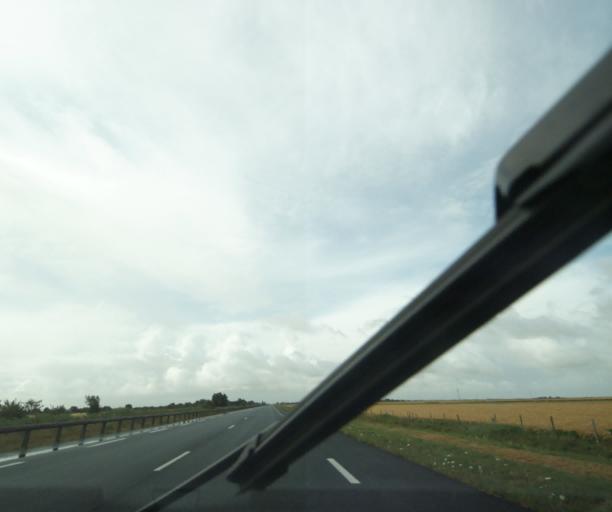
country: FR
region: Pays de la Loire
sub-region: Departement de la Vendee
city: Champagne-les-Marais
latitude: 46.3670
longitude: -1.0886
